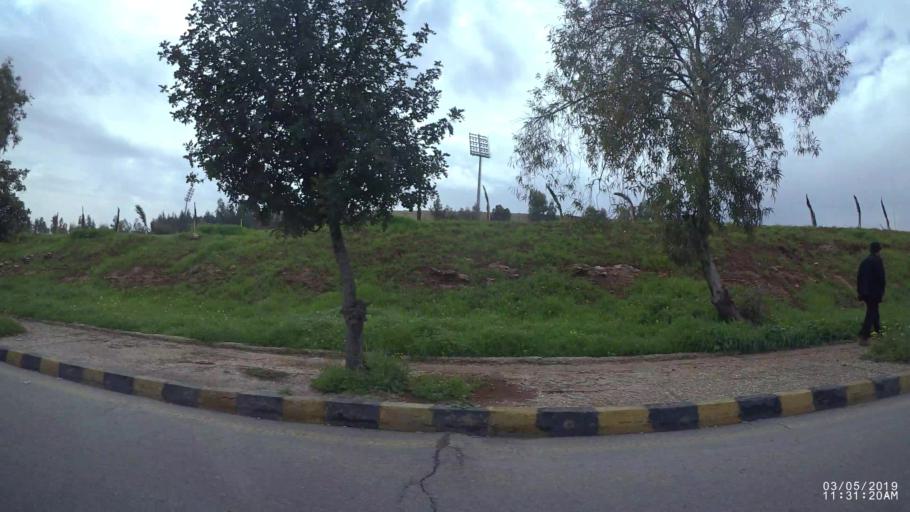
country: JO
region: Amman
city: Amman
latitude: 31.9695
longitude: 35.9426
